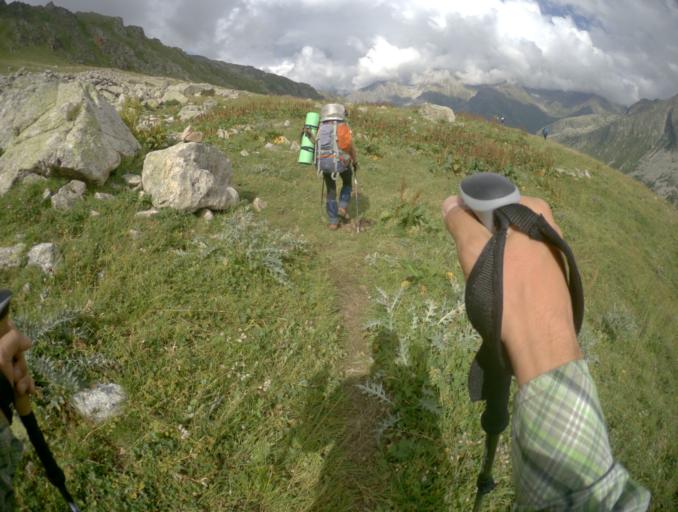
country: RU
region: Karachayevo-Cherkesiya
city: Uchkulan
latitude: 43.2676
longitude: 42.1292
